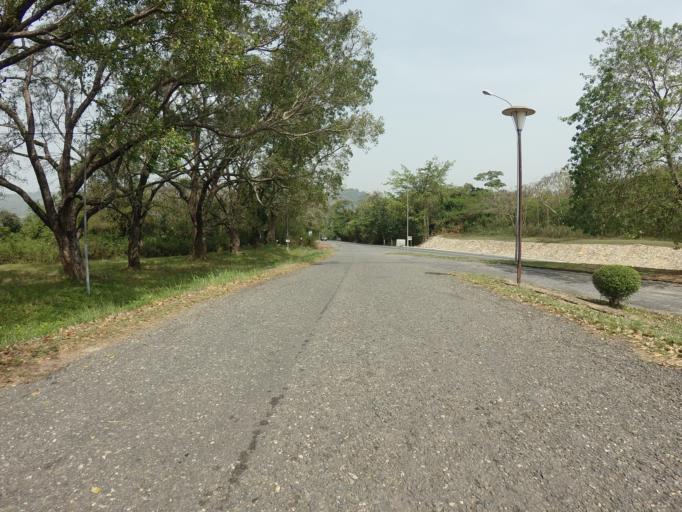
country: GH
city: Akropong
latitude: 6.2648
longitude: 0.0582
